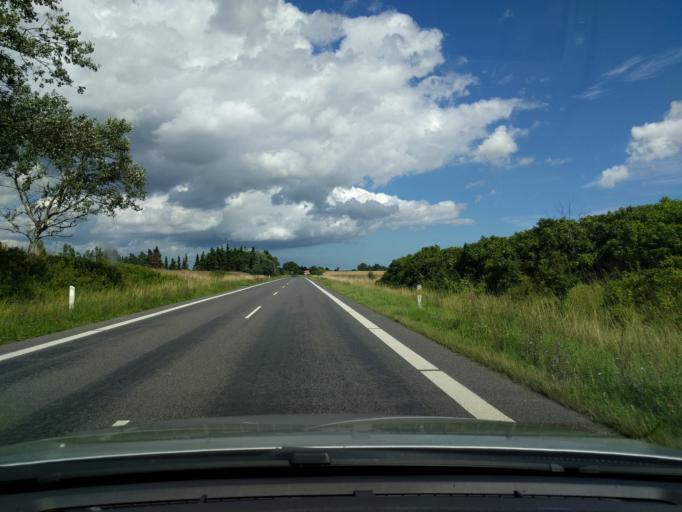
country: DK
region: Zealand
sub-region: Guldborgsund Kommune
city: Stubbekobing
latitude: 54.9164
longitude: 12.1464
